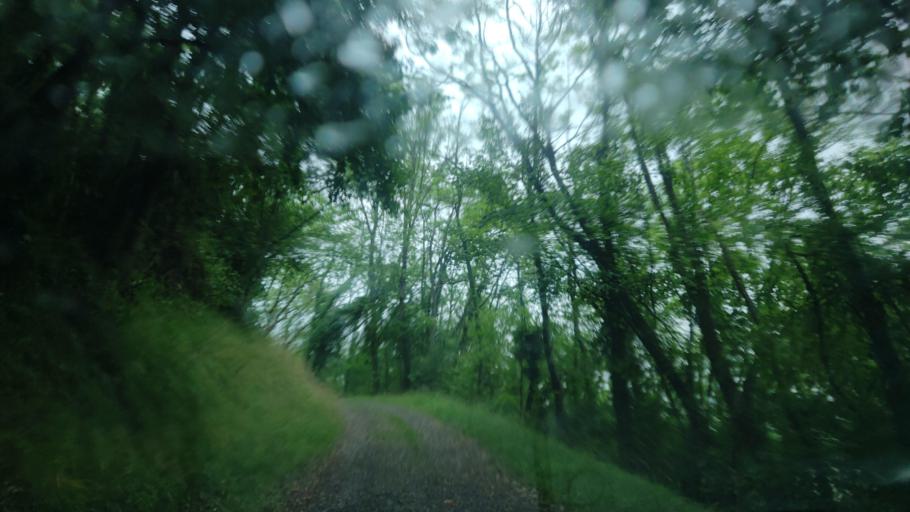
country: FR
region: Rhone-Alpes
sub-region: Departement de la Savoie
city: Coise-Saint-Jean-Pied-Gauthier
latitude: 45.4971
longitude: 6.1420
